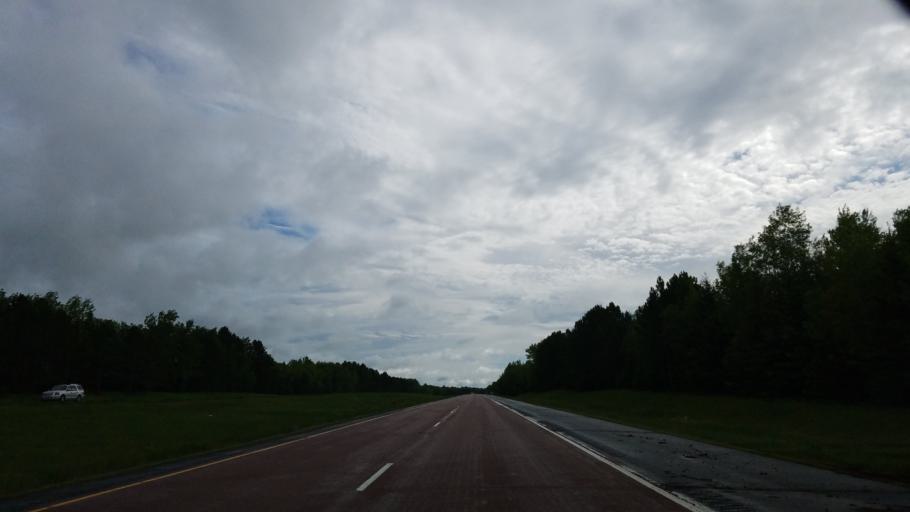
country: US
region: Minnesota
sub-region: Lake County
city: Two Harbors
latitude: 46.9189
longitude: -91.8686
